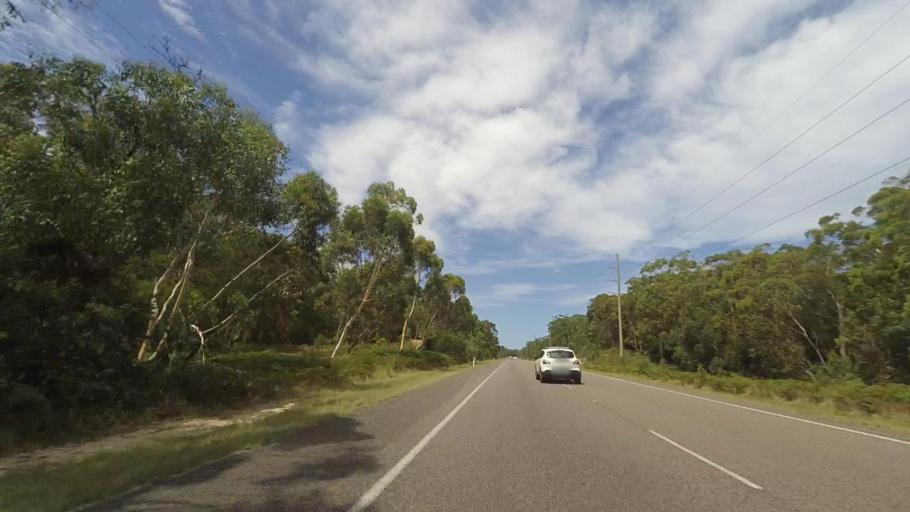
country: AU
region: New South Wales
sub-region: Port Stephens Shire
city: Medowie
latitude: -32.7908
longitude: 151.9564
